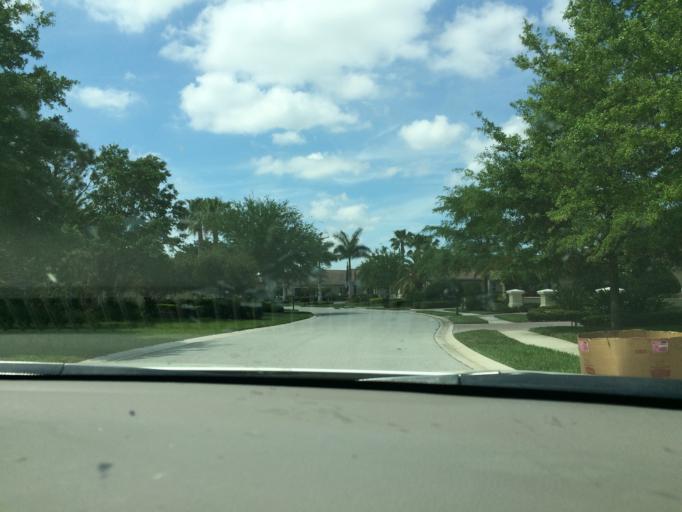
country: US
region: Florida
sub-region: Manatee County
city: Ellenton
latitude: 27.5104
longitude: -82.4399
